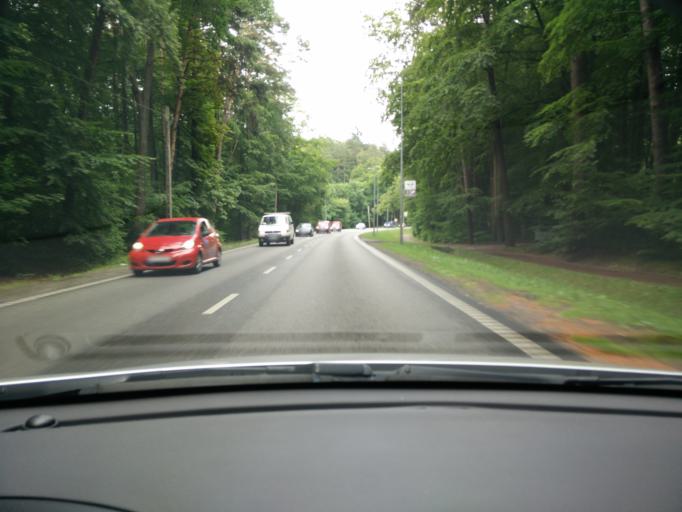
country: PL
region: Pomeranian Voivodeship
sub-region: Sopot
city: Sopot
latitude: 54.4164
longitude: 18.5439
